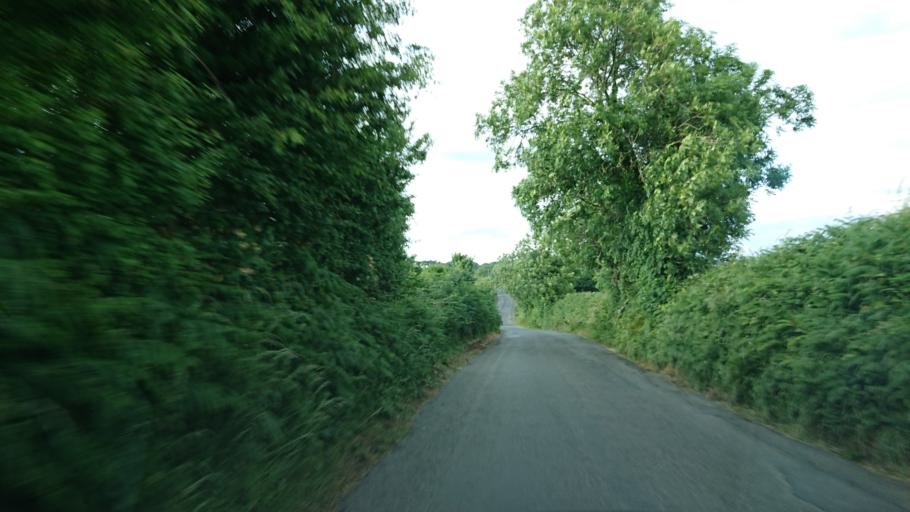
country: IE
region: Munster
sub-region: Waterford
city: Tra Mhor
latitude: 52.2190
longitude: -7.1844
